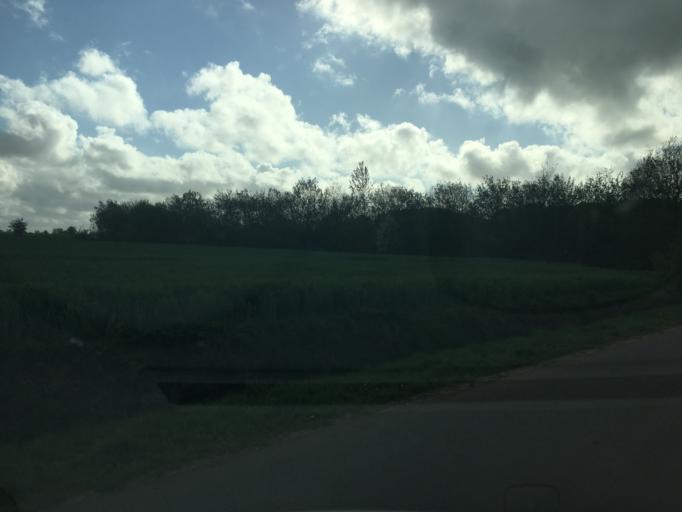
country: DE
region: Schleswig-Holstein
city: Aventoft
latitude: 55.0080
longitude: 8.7803
